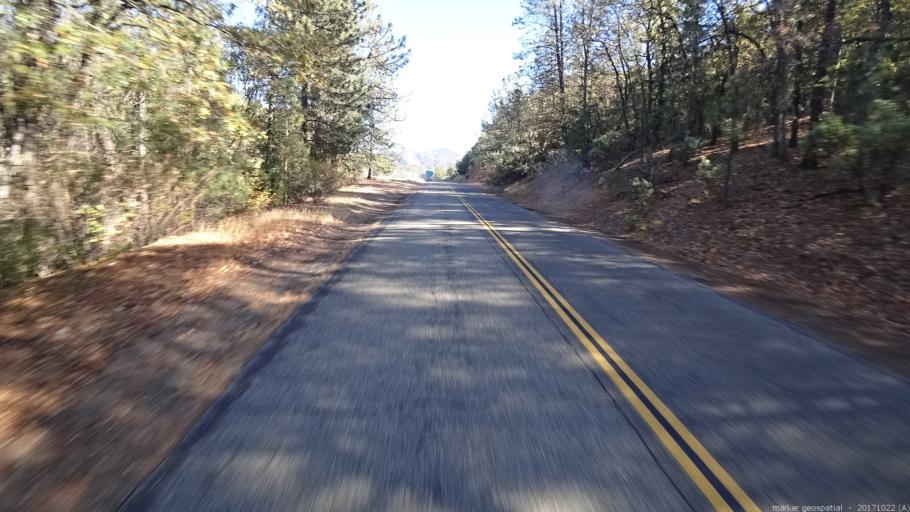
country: US
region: California
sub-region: Shasta County
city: Shasta Lake
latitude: 40.8661
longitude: -122.3655
